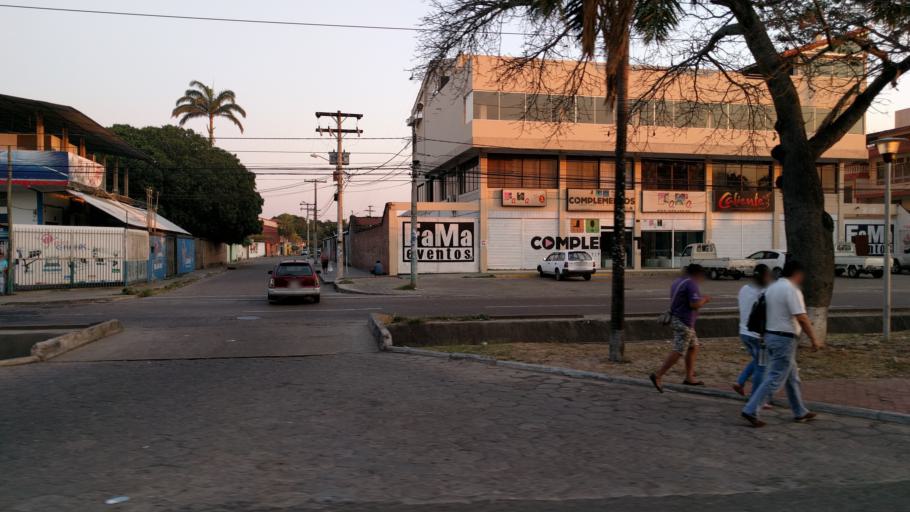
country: BO
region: Santa Cruz
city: Santa Cruz de la Sierra
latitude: -17.7850
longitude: -63.1980
